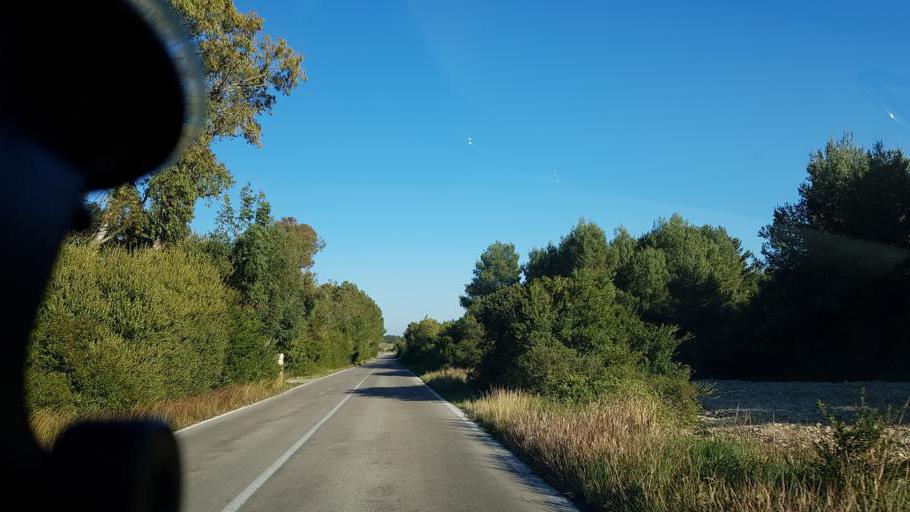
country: IT
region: Apulia
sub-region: Provincia di Lecce
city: Struda
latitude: 40.3899
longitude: 18.2904
